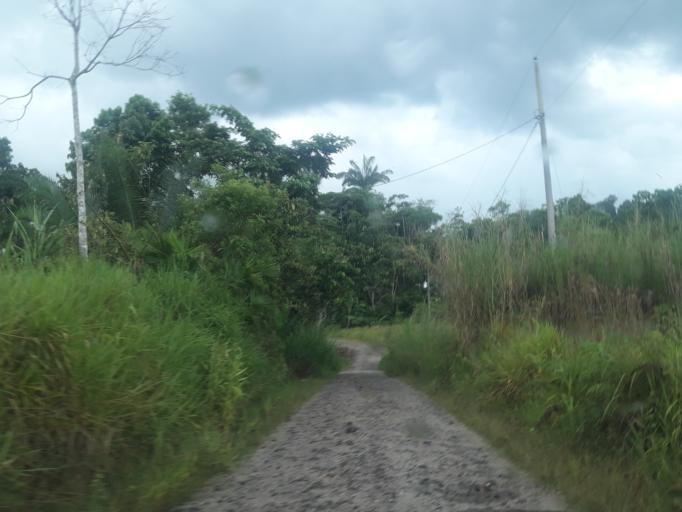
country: EC
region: Napo
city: Tena
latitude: -1.1008
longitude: -77.6883
